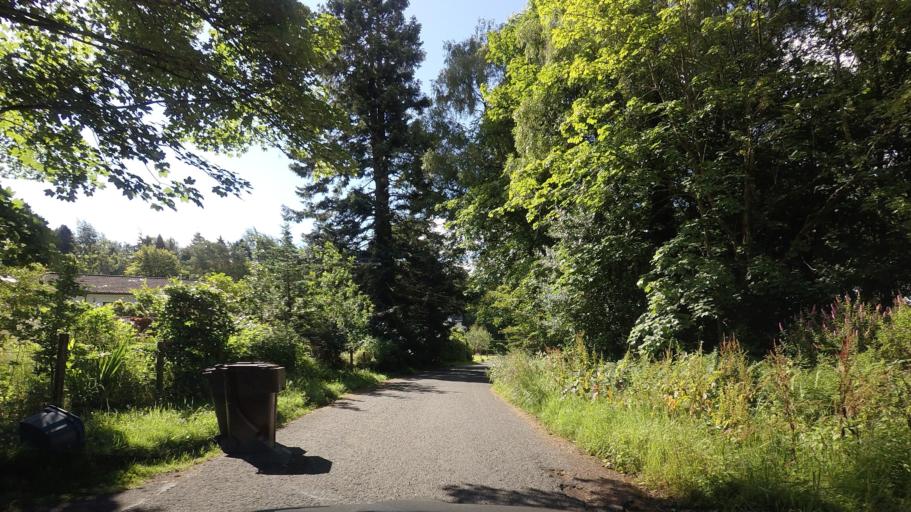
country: GB
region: Scotland
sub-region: Stirling
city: Killearn
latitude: 56.0665
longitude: -4.4759
